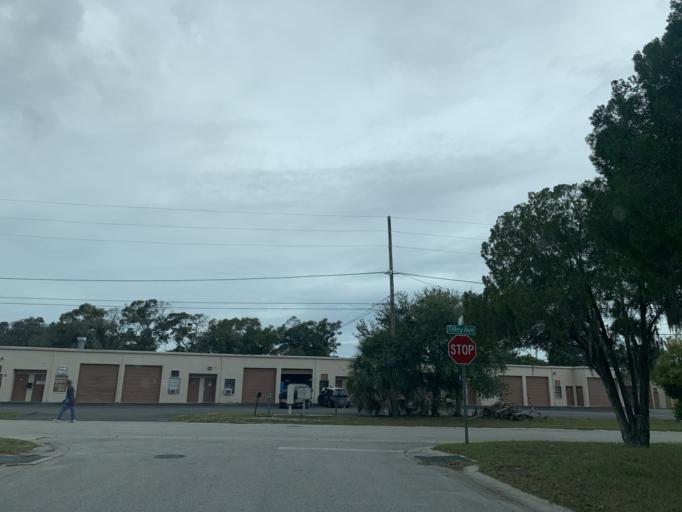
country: US
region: Florida
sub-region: Pinellas County
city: Belleair
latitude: 27.9361
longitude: -82.7933
